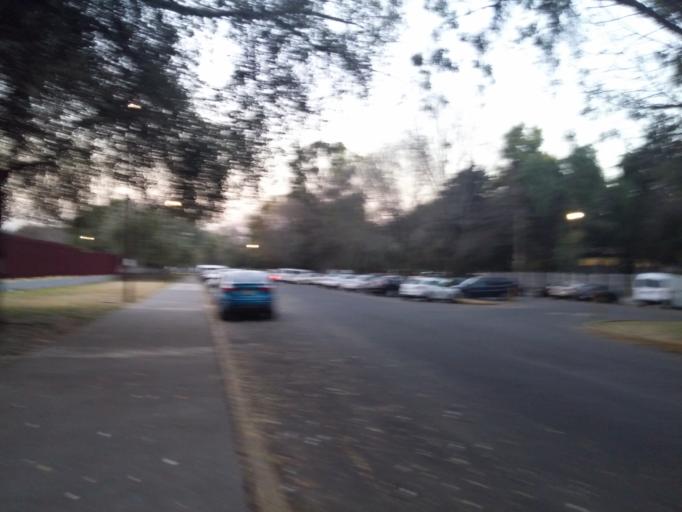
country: MX
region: Mexico
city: Colonia Lindavista
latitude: 19.4986
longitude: -99.1399
